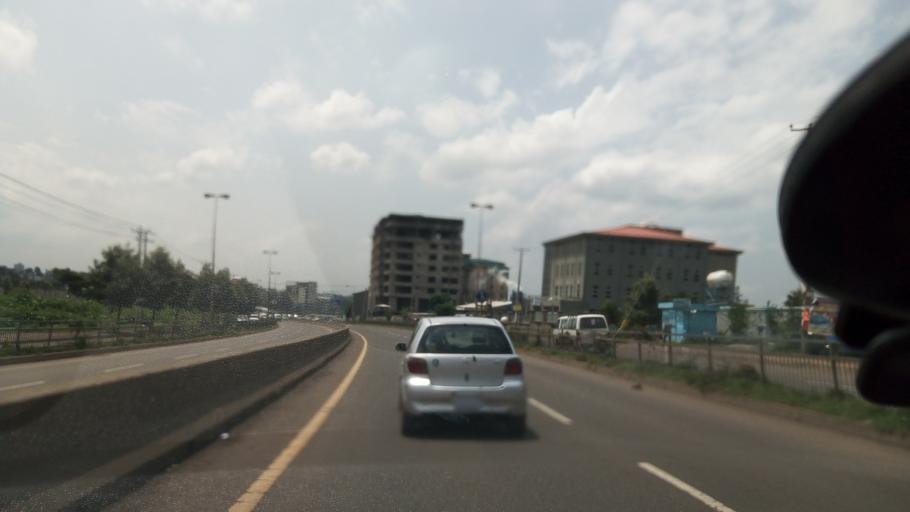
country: ET
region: Adis Abeba
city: Addis Ababa
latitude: 8.9646
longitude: 38.7297
